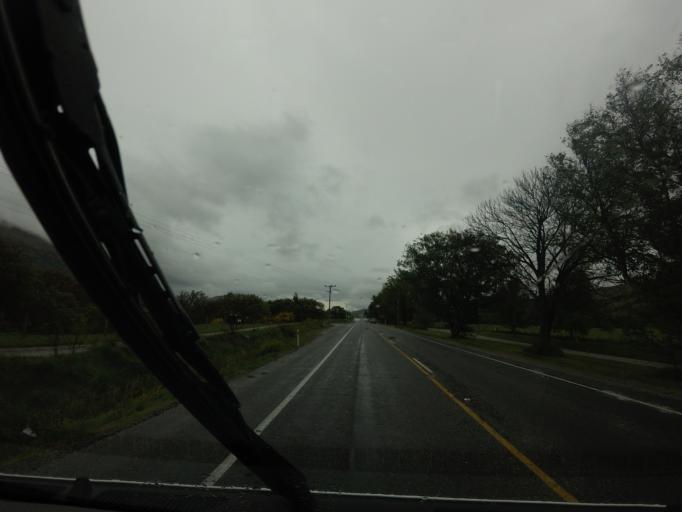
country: NZ
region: Otago
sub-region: Queenstown-Lakes District
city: Arrowtown
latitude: -44.9942
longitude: 168.7960
